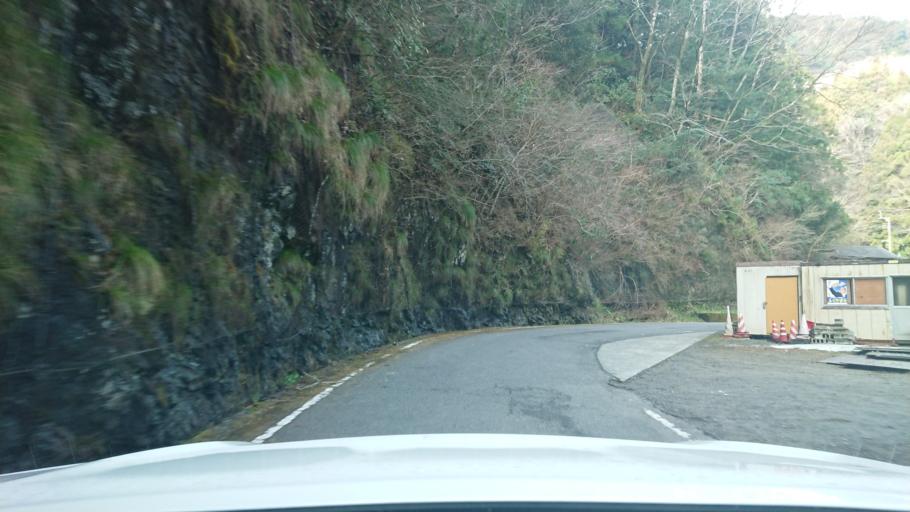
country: JP
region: Tokushima
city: Ishii
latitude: 33.8957
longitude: 134.3982
